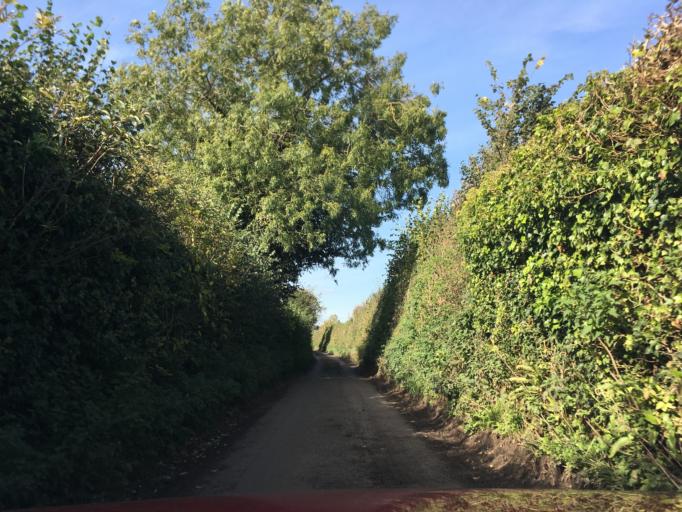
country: GB
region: England
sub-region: South Gloucestershire
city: Charfield
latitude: 51.6133
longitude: -2.4334
